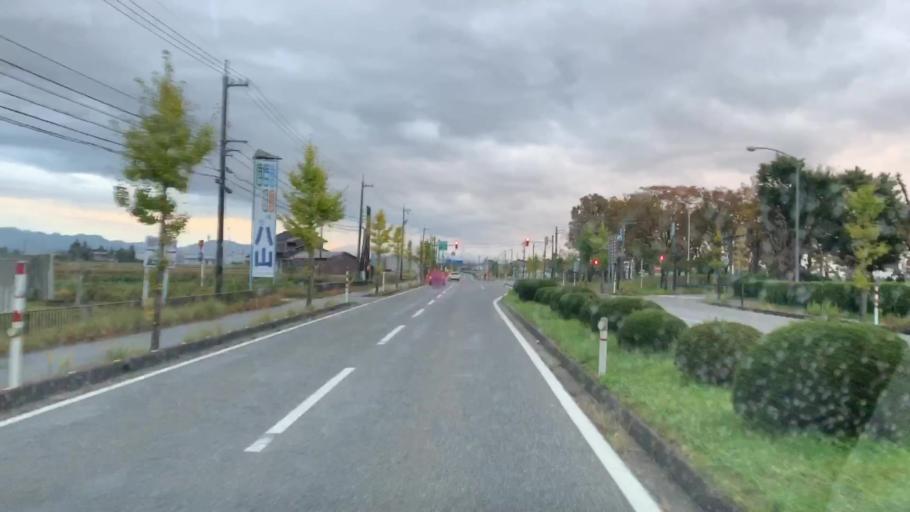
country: JP
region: Toyama
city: Kamiichi
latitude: 36.6830
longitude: 137.3314
